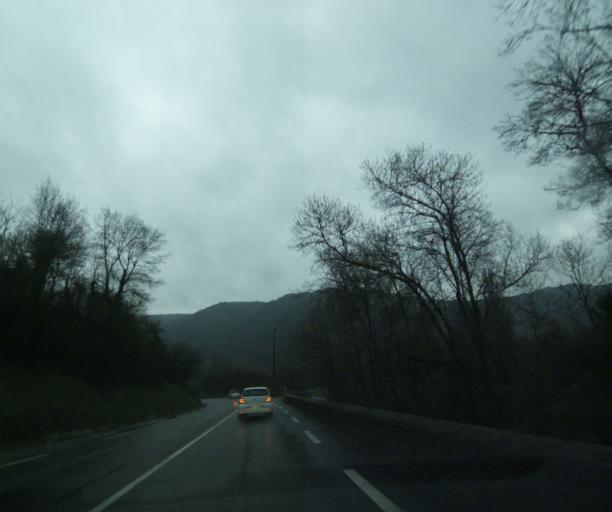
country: FR
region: Rhone-Alpes
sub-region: Departement de l'Ardeche
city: Saint-Julien-en-Saint-Alban
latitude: 44.7525
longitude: 4.6859
